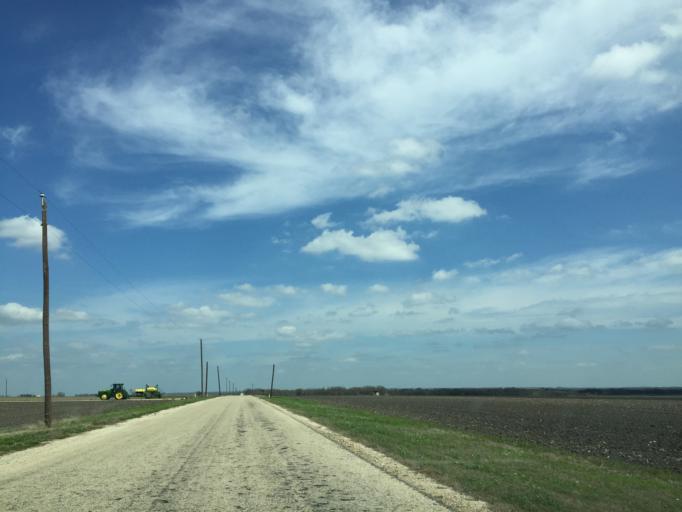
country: US
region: Texas
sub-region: Milam County
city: Thorndale
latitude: 30.5489
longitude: -97.2719
